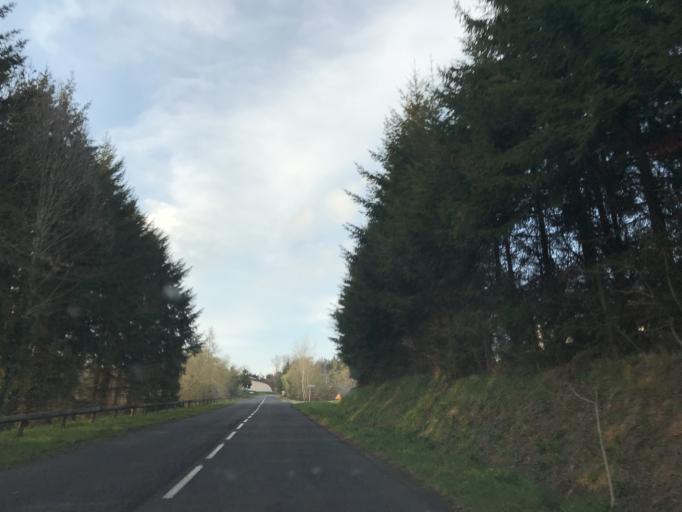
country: FR
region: Auvergne
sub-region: Departement du Puy-de-Dome
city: Saint-Remy-sur-Durolle
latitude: 45.8759
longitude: 3.5911
